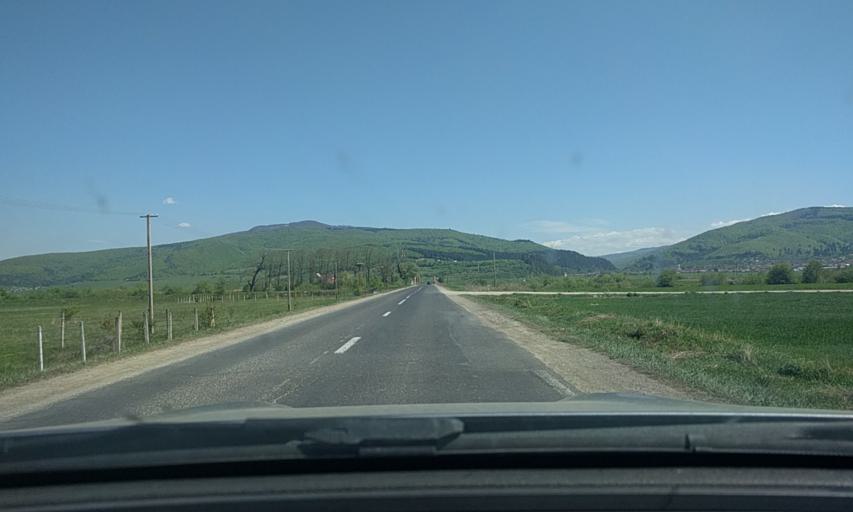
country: RO
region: Brasov
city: Tunelu-Teliu
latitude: 45.7114
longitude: 25.8238
